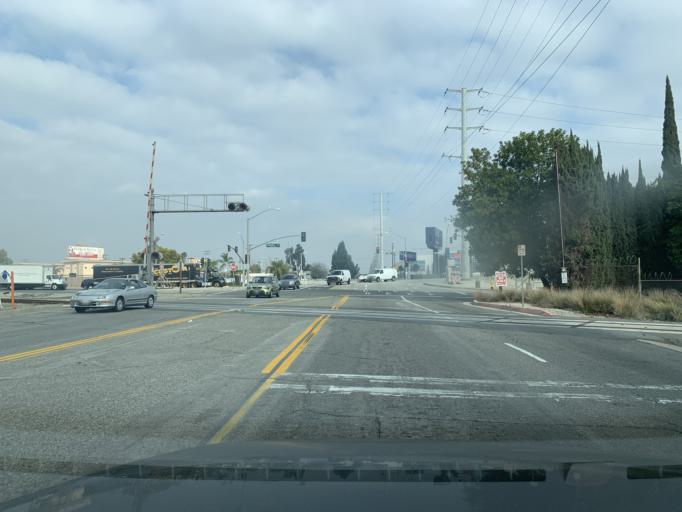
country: US
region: California
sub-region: Los Angeles County
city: Cerritos
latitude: 33.8871
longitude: -118.0378
